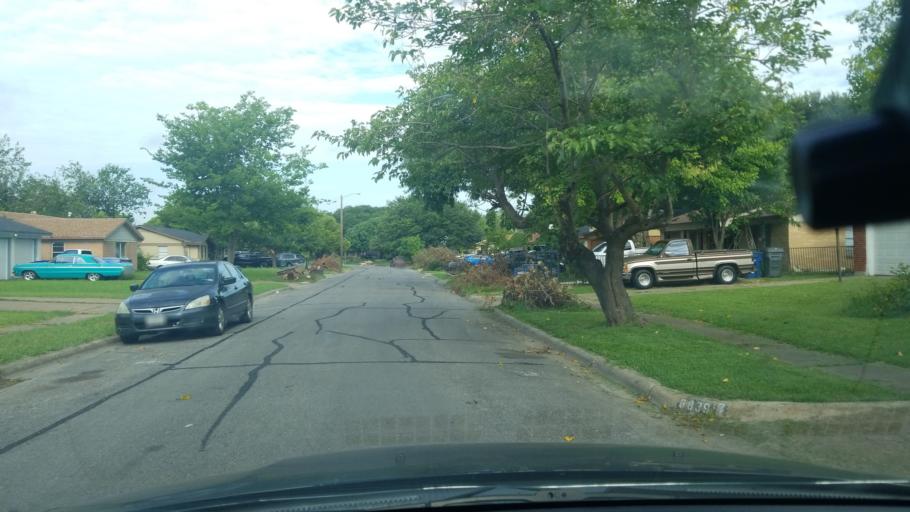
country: US
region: Texas
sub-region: Dallas County
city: Balch Springs
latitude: 32.7478
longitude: -96.6709
